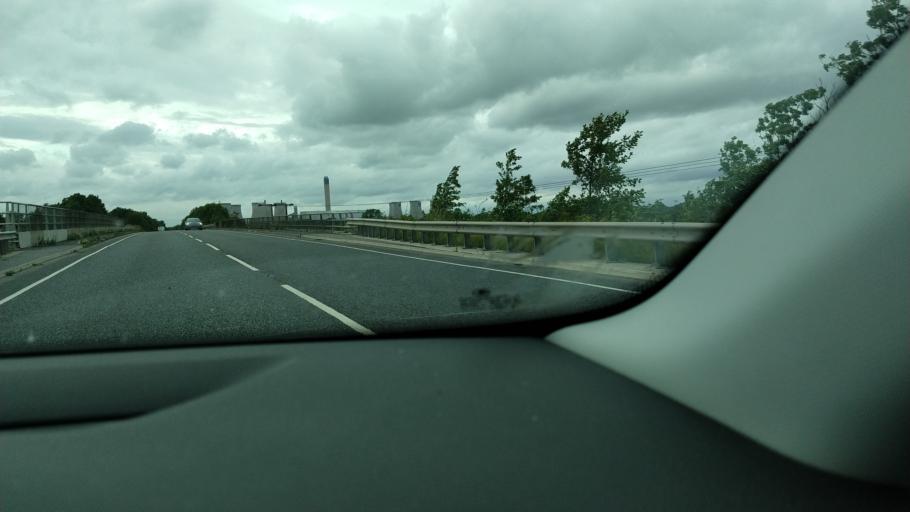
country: GB
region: England
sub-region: East Riding of Yorkshire
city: Rawcliffe
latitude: 53.7141
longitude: -0.9576
